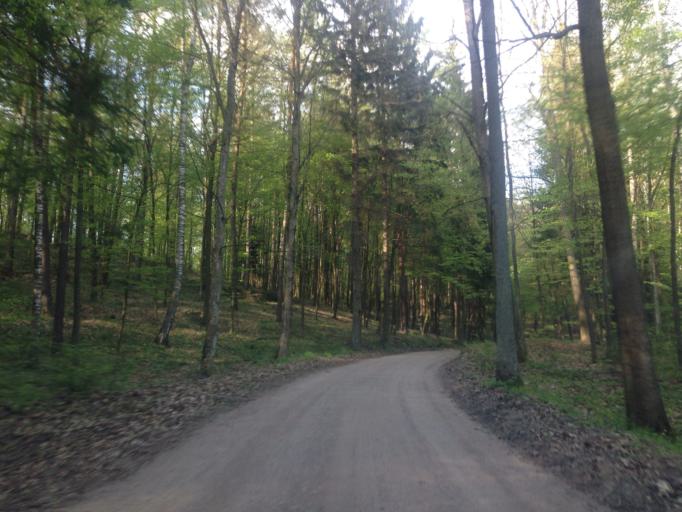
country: PL
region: Kujawsko-Pomorskie
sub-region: Powiat brodnicki
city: Gorzno
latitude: 53.2122
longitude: 19.7267
